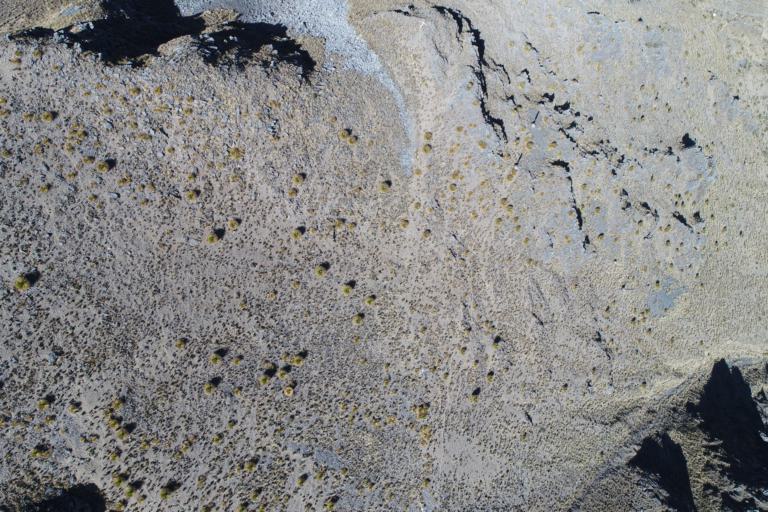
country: BO
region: La Paz
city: Viloco
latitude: -16.8068
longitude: -67.5470
